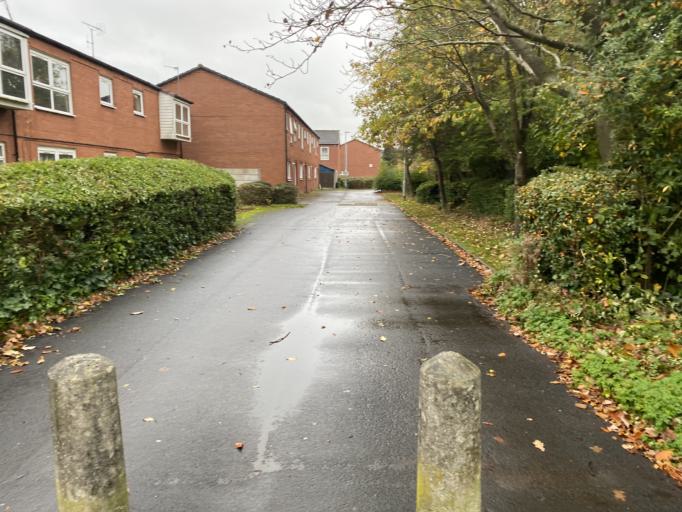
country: GB
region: England
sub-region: Warrington
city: Great Sankey
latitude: 53.3918
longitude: -2.6292
